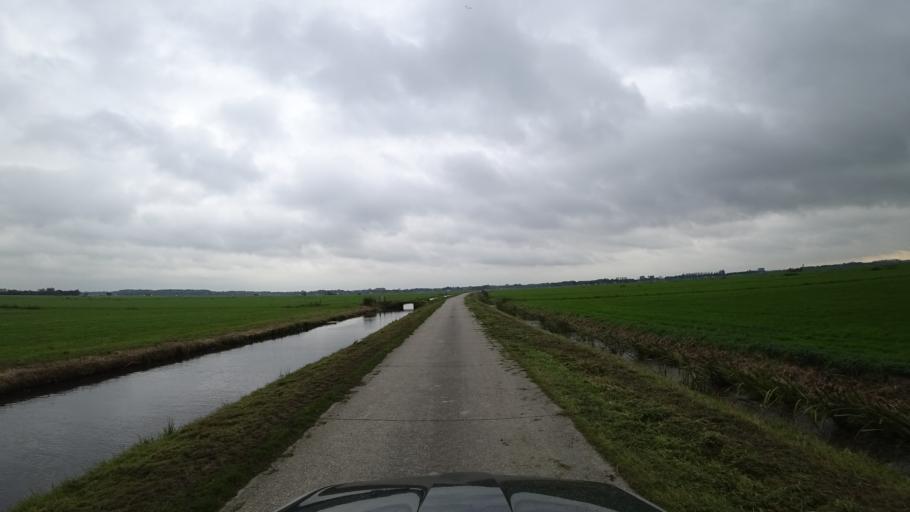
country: NL
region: Gelderland
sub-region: Gemeente Nijkerk
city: Nijkerk
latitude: 52.2596
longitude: 5.4953
